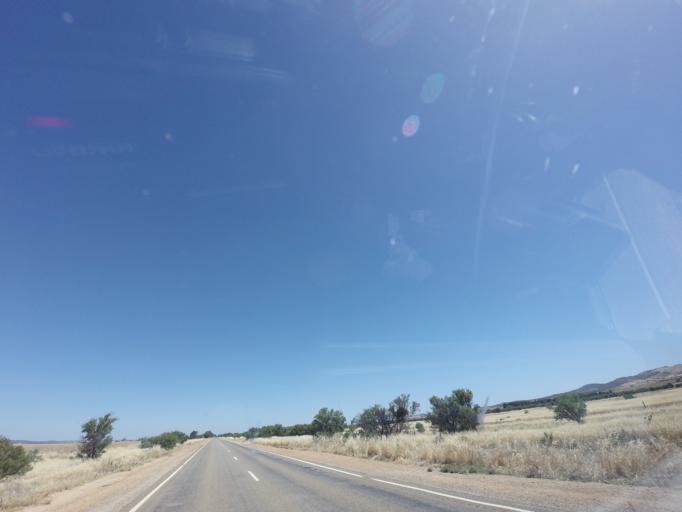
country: AU
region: South Australia
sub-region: Peterborough
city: Peterborough
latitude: -32.8043
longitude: 138.6815
